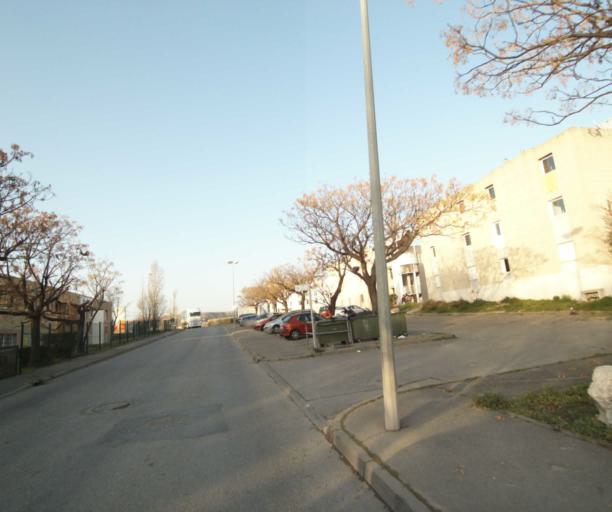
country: FR
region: Provence-Alpes-Cote d'Azur
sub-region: Departement des Bouches-du-Rhone
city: Saint-Victoret
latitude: 43.4204
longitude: 5.2665
